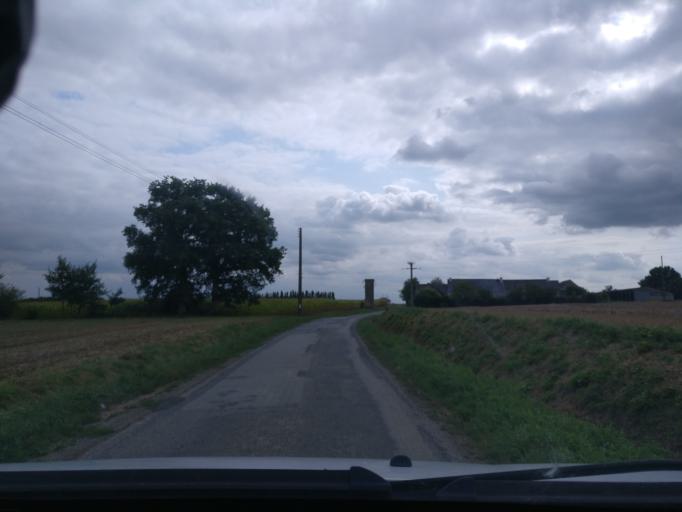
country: FR
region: Brittany
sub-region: Departement d'Ille-et-Vilaine
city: Nouvoitou
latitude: 48.0737
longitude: -1.5347
